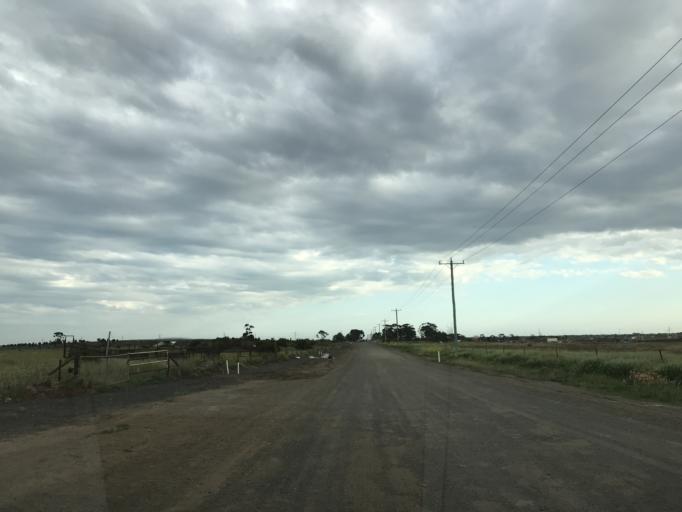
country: AU
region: Victoria
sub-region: Wyndham
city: Truganina
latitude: -37.8161
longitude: 144.7223
